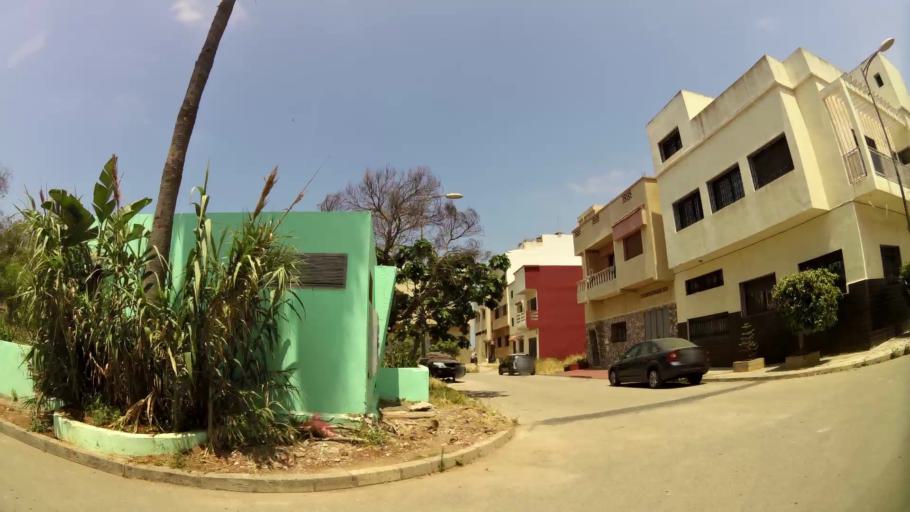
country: MA
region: Rabat-Sale-Zemmour-Zaer
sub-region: Skhirate-Temara
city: Temara
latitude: 33.9786
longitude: -6.8952
